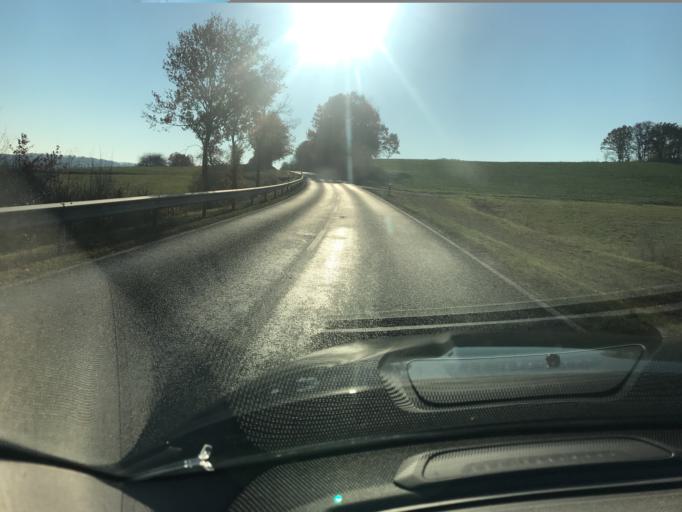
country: DE
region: Rheinland-Pfalz
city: Nomborn
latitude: 50.4365
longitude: 7.9330
